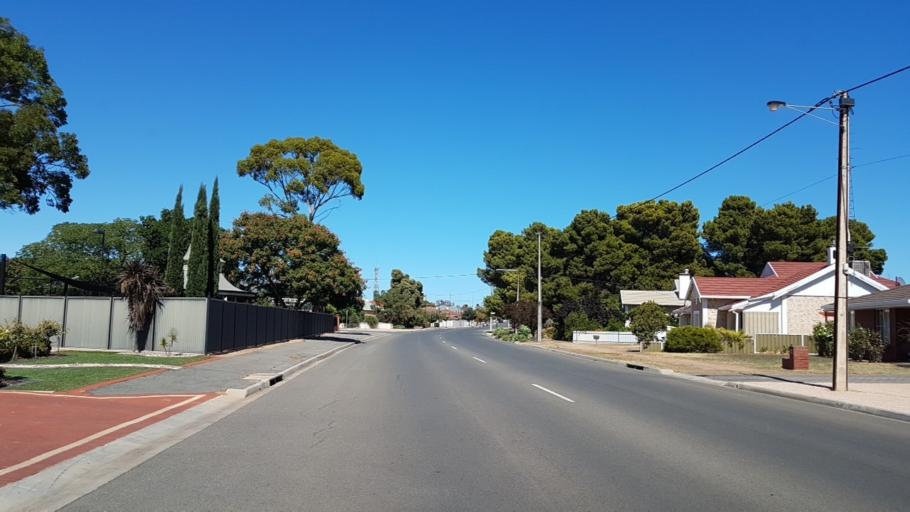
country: AU
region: South Australia
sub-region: Copper Coast
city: Kadina
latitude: -33.9606
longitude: 137.7241
